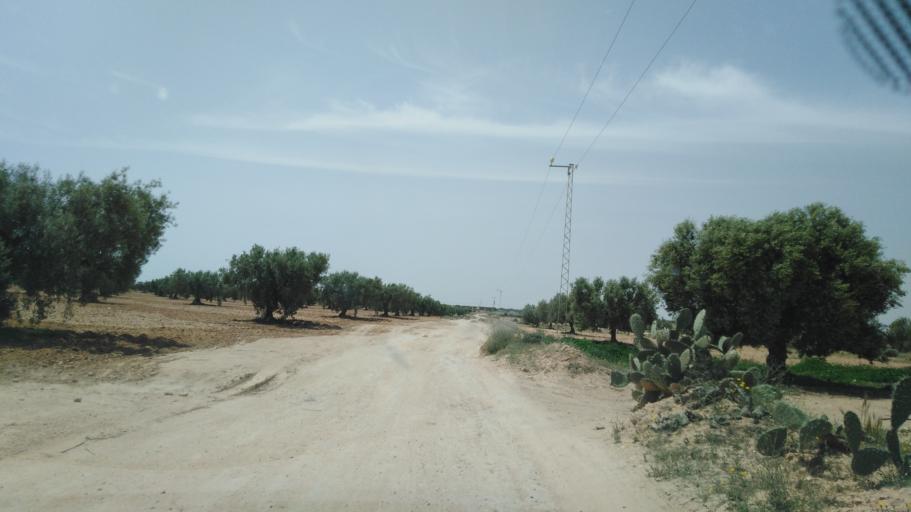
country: TN
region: Safaqis
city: Sfax
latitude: 34.7212
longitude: 10.5727
